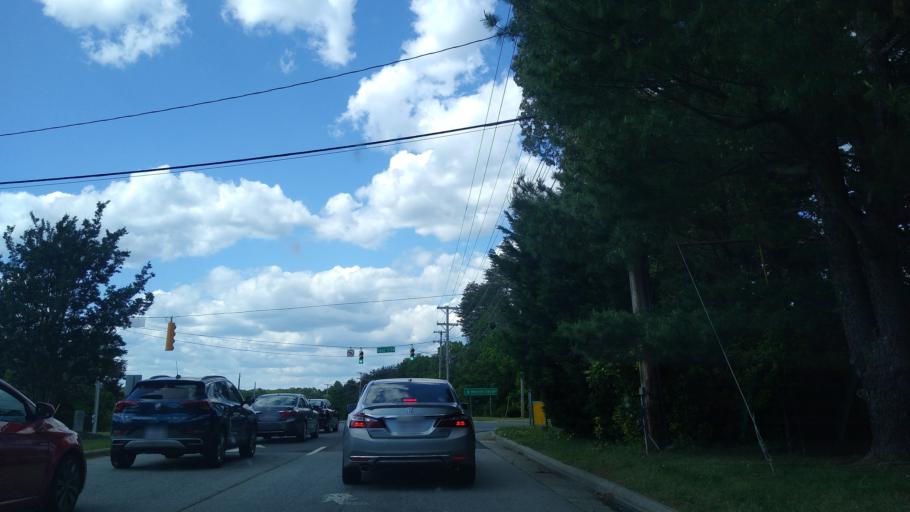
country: US
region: North Carolina
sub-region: Guilford County
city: High Point
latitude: 36.0079
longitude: -80.0099
